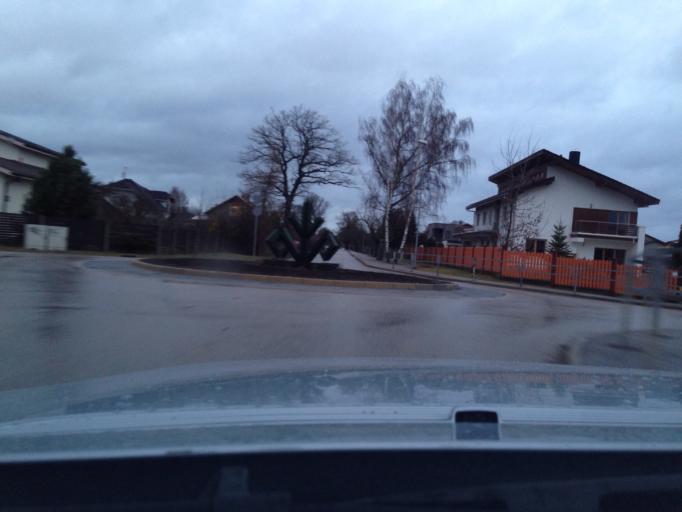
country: LV
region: Marupe
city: Marupe
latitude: 56.9132
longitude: 24.0376
